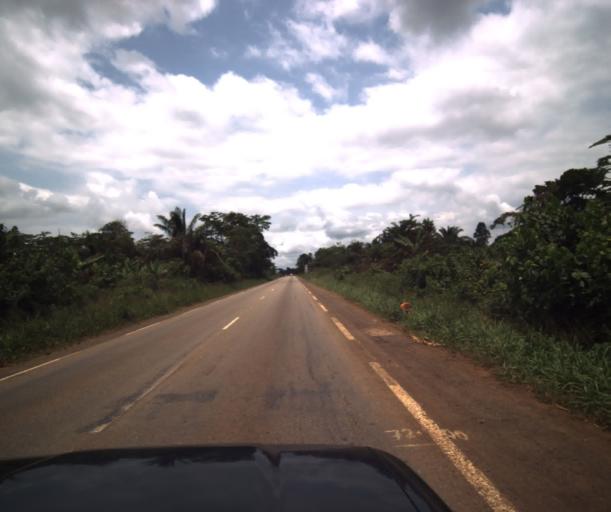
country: CM
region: Centre
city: Eseka
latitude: 3.8563
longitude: 10.9384
